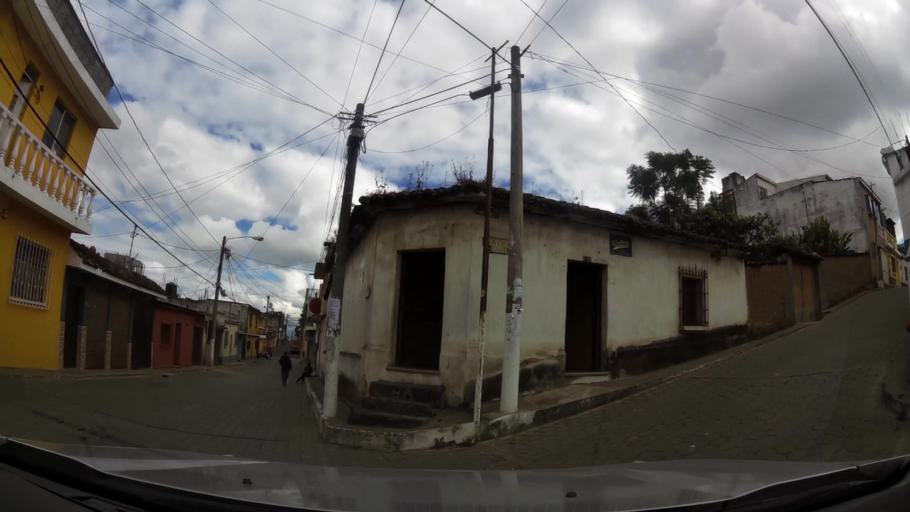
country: GT
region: Guatemala
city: Mixco
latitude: 14.6331
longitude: -90.6077
